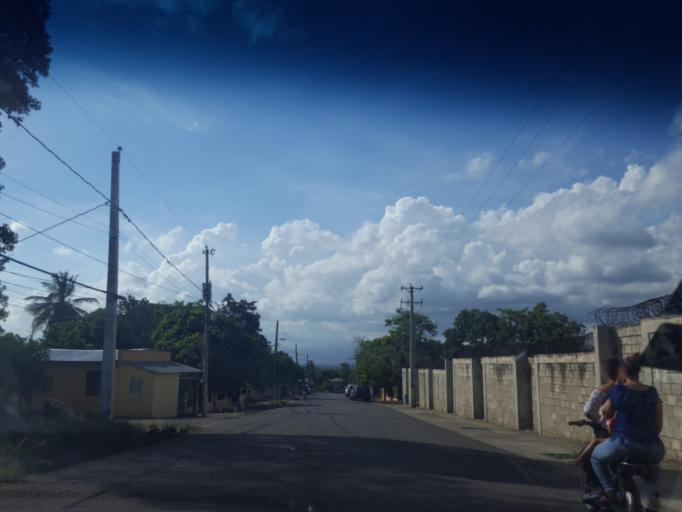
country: DO
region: Santiago
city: Licey al Medio
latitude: 19.3701
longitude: -70.6073
